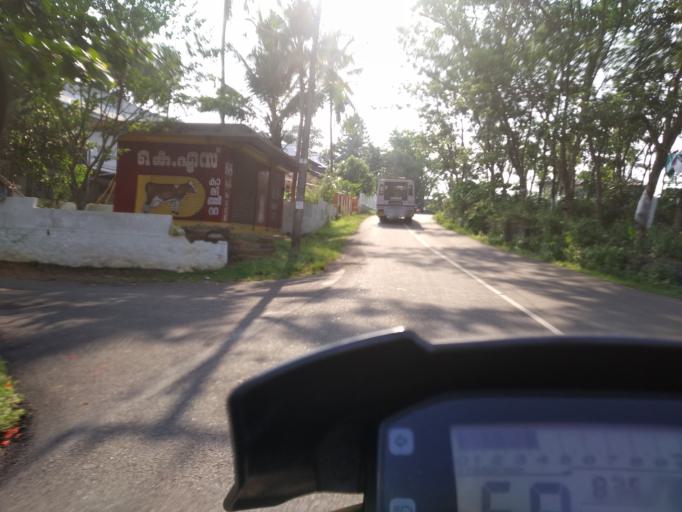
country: IN
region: Kerala
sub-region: Ernakulam
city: Ramamangalam
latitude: 9.9145
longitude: 76.4324
